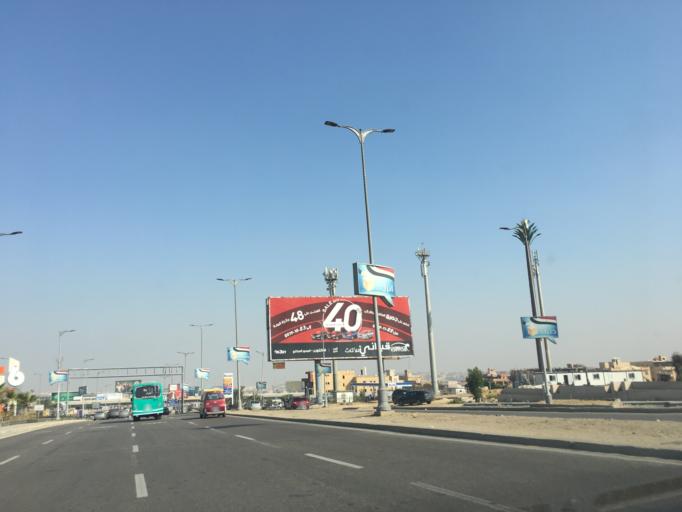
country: EG
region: Al Jizah
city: Awsim
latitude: 30.0062
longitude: 30.9785
